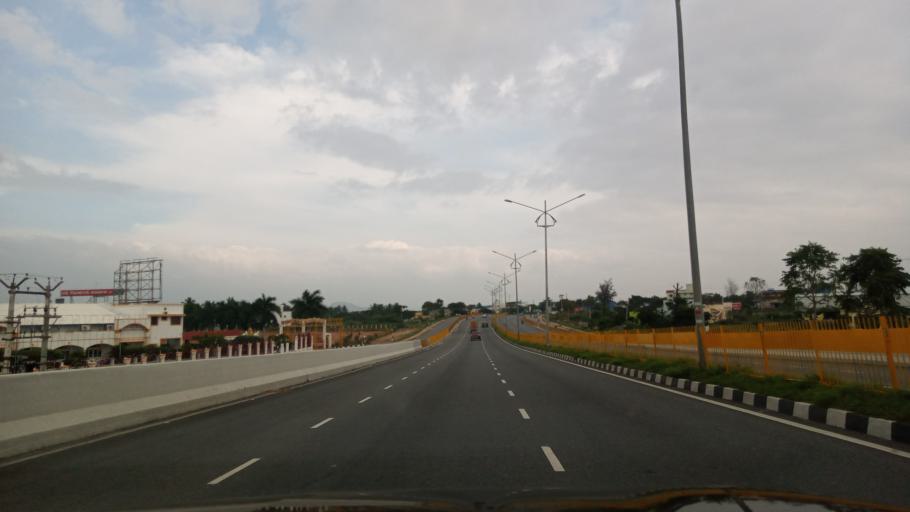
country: IN
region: Tamil Nadu
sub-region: Krishnagiri
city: Krishnagiri
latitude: 12.5356
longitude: 78.2511
